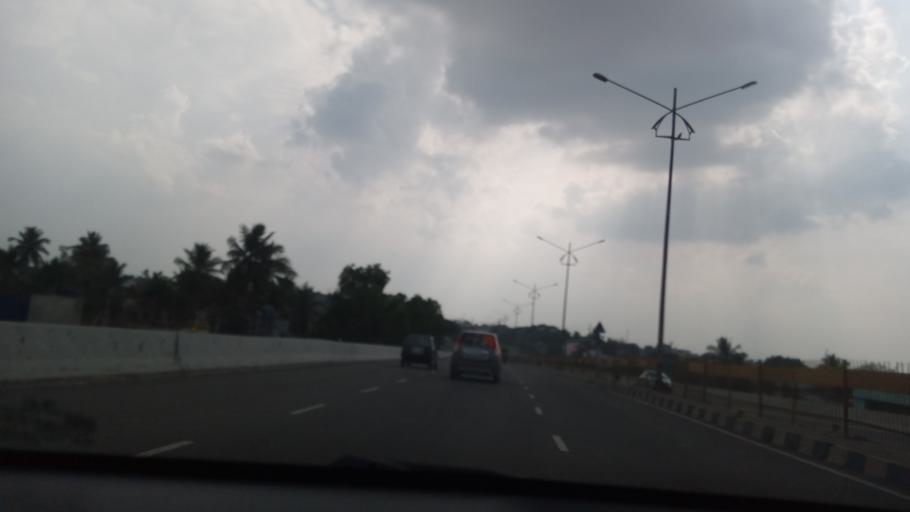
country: IN
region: Tamil Nadu
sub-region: Vellore
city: Vaniyambadi
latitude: 12.6823
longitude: 78.6285
